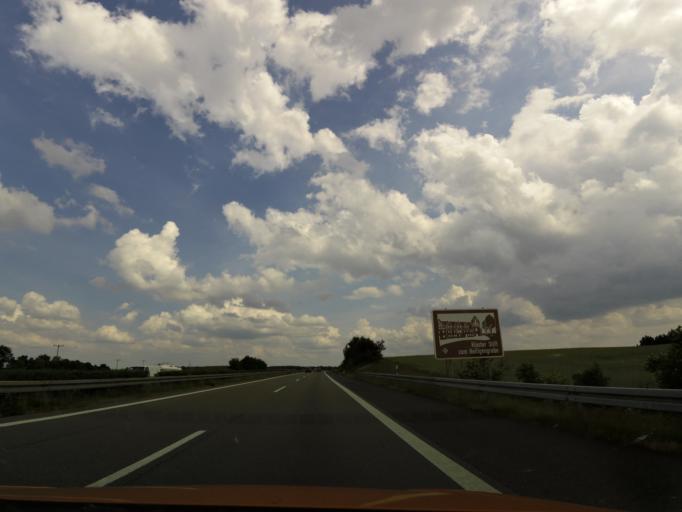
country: DE
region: Brandenburg
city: Heiligengrabe
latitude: 53.1689
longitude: 12.3612
